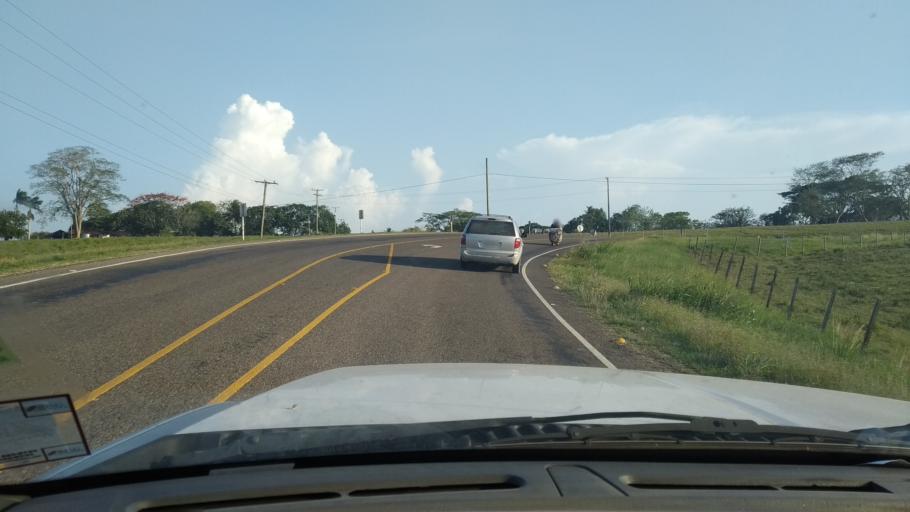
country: BZ
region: Cayo
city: San Ignacio
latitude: 17.2453
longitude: -88.9875
